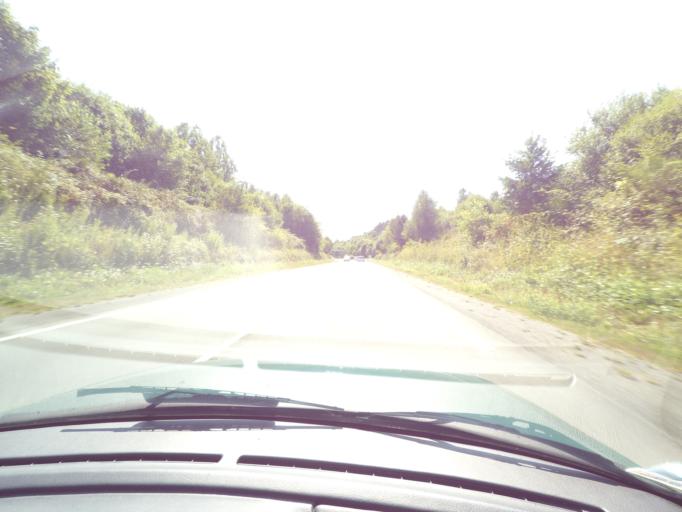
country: FR
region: Limousin
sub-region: Departement de la Haute-Vienne
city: Chaptelat
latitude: 45.8949
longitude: 1.2478
